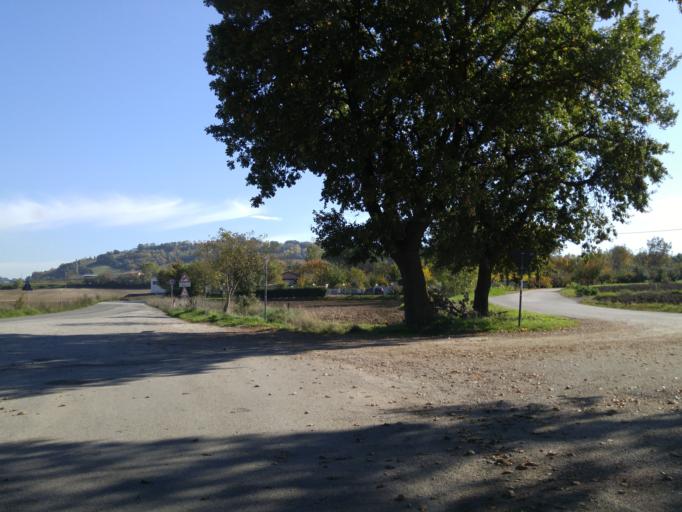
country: IT
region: The Marches
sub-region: Provincia di Pesaro e Urbino
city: Tavernelle
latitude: 43.7229
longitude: 12.8928
